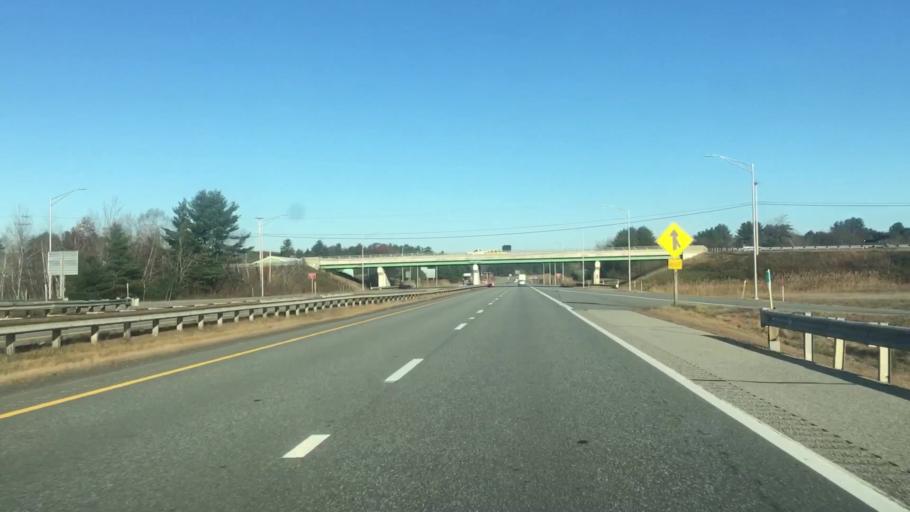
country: US
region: Maine
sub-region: Cumberland County
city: New Gloucester
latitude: 43.8819
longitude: -70.3351
